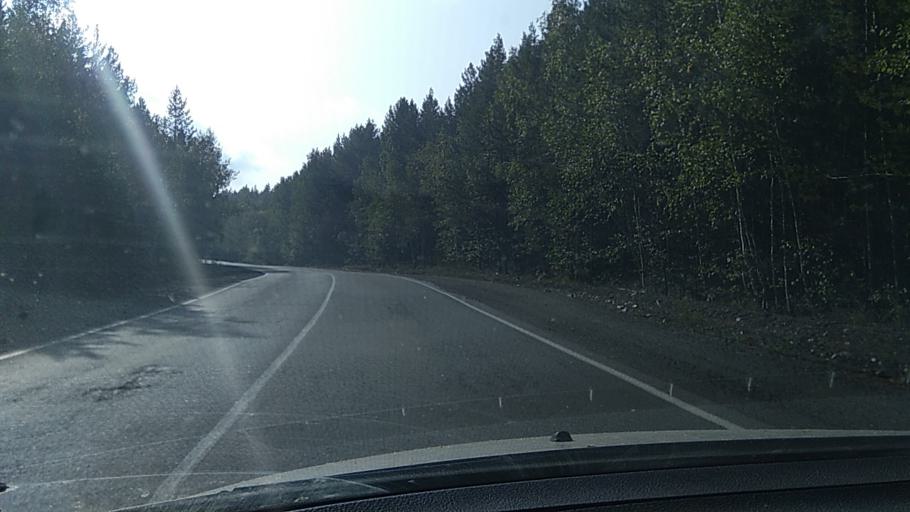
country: RU
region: Chelyabinsk
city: Karabash
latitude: 55.4273
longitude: 60.2584
